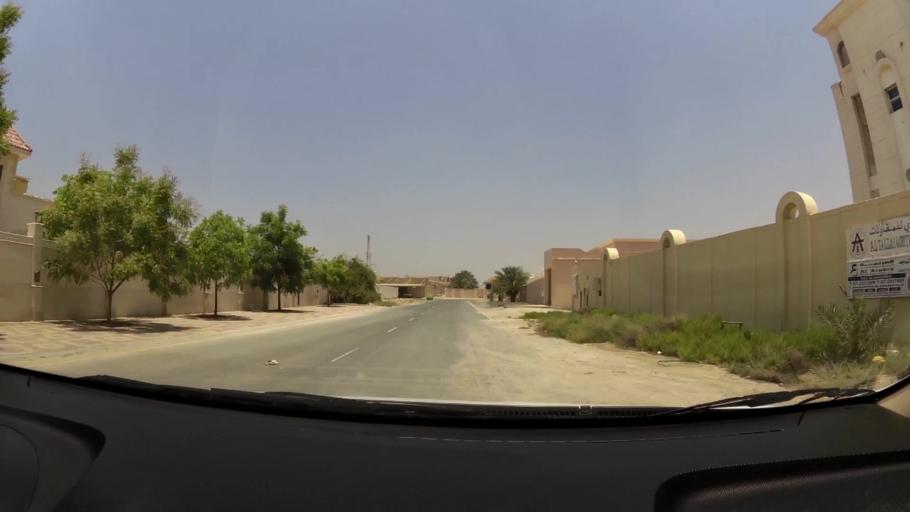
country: AE
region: Umm al Qaywayn
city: Umm al Qaywayn
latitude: 25.5341
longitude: 55.5405
